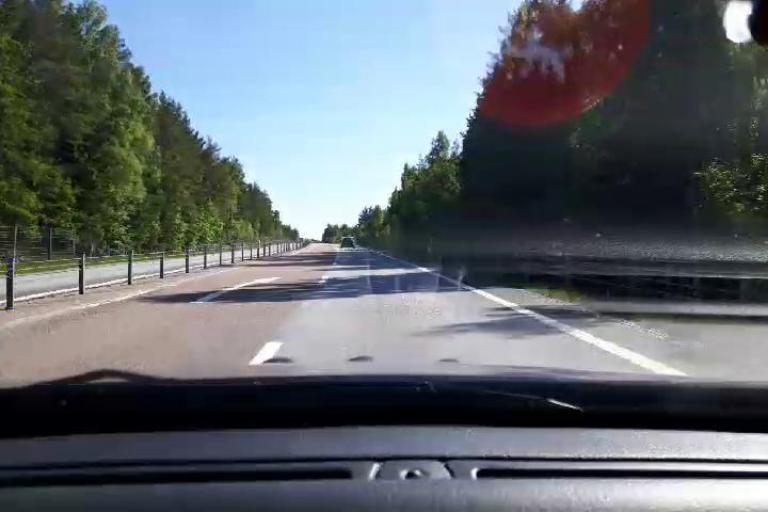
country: SE
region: Gaevleborg
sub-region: Soderhamns Kommun
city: Ljusne
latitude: 61.1271
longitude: 17.0153
